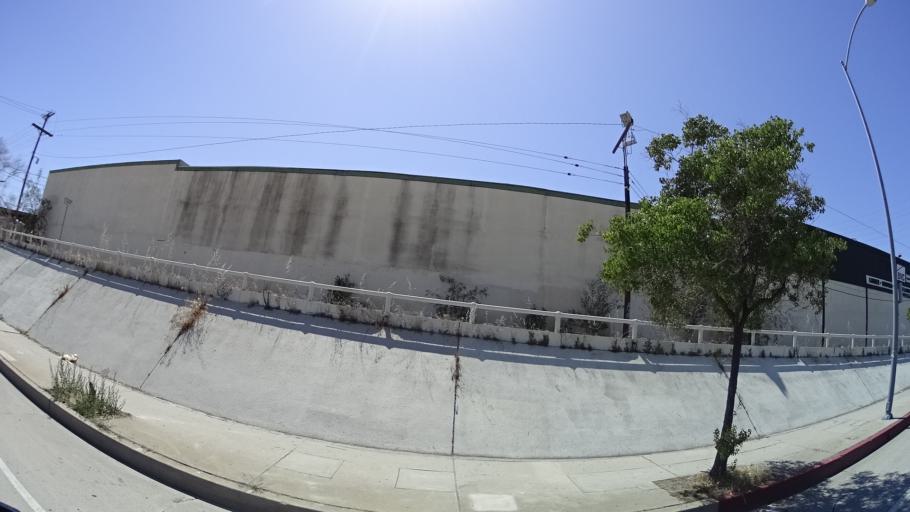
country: US
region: California
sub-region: Los Angeles County
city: North Hollywood
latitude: 34.2007
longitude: -118.3879
